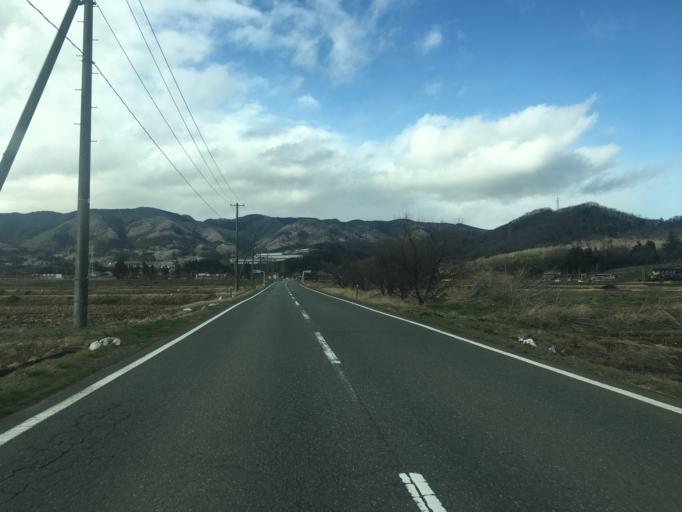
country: JP
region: Fukushima
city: Yanagawamachi-saiwaicho
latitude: 37.8843
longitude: 140.5909
